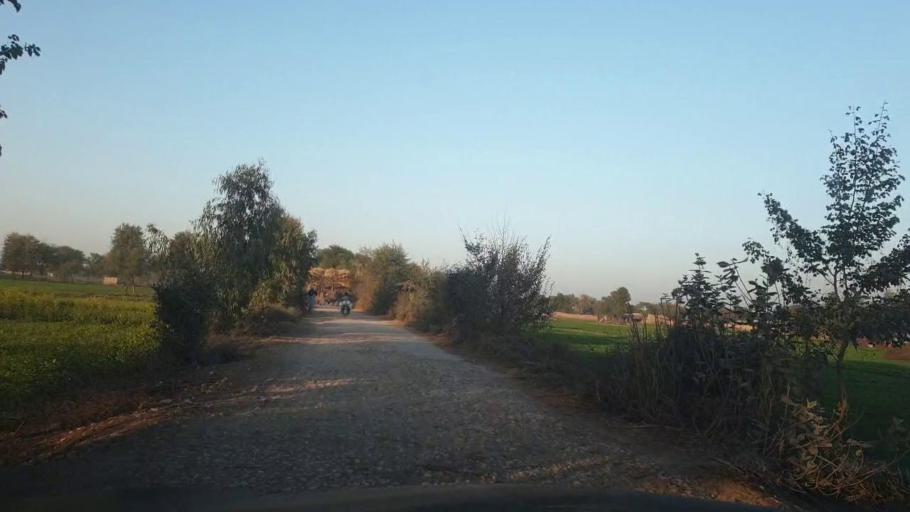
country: PK
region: Sindh
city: Ubauro
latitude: 28.1761
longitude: 69.6033
